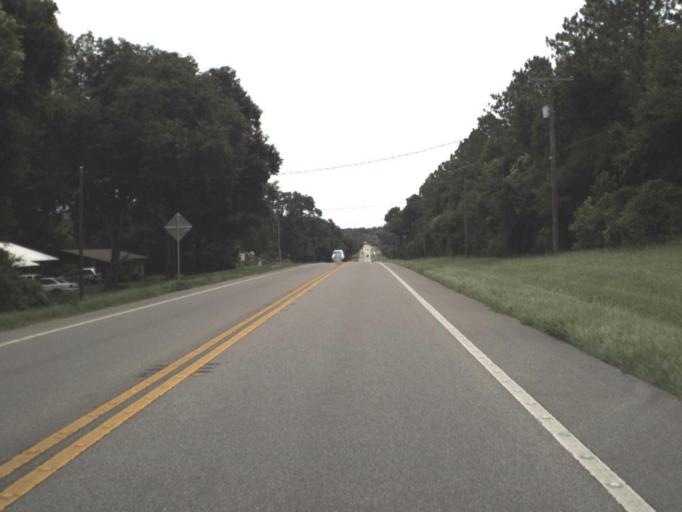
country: US
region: Florida
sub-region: Pasco County
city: Saint Leo
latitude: 28.3423
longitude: -82.2293
